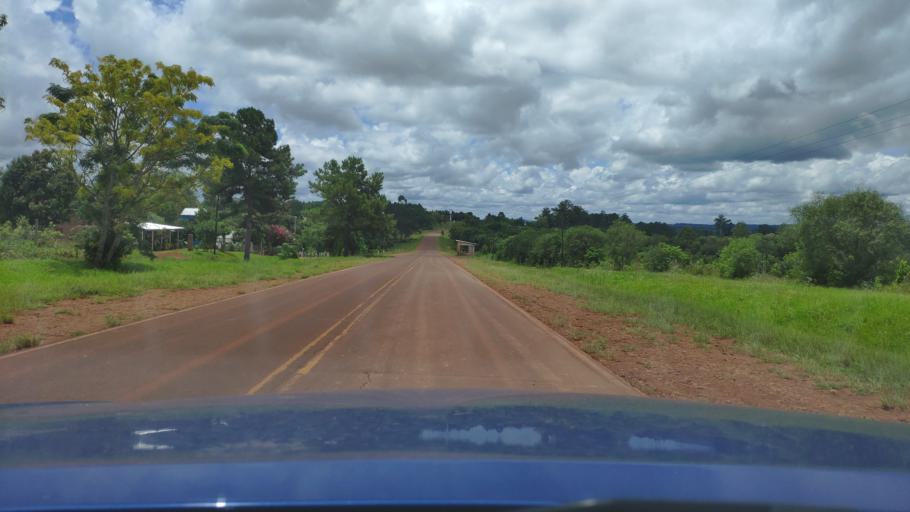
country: AR
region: Misiones
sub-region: Departamento de San Javier
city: San Javier
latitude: -27.8612
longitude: -55.2543
